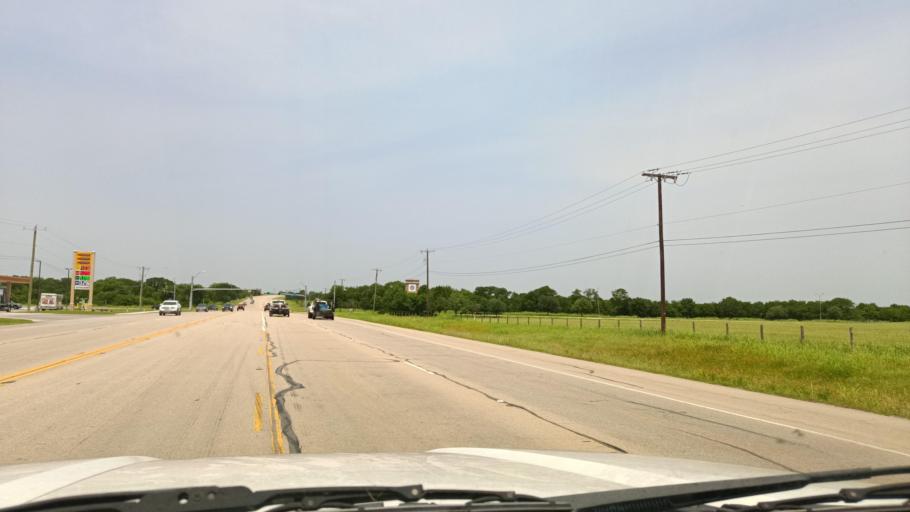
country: US
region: Texas
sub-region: Bell County
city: Temple
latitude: 31.1280
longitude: -97.3978
